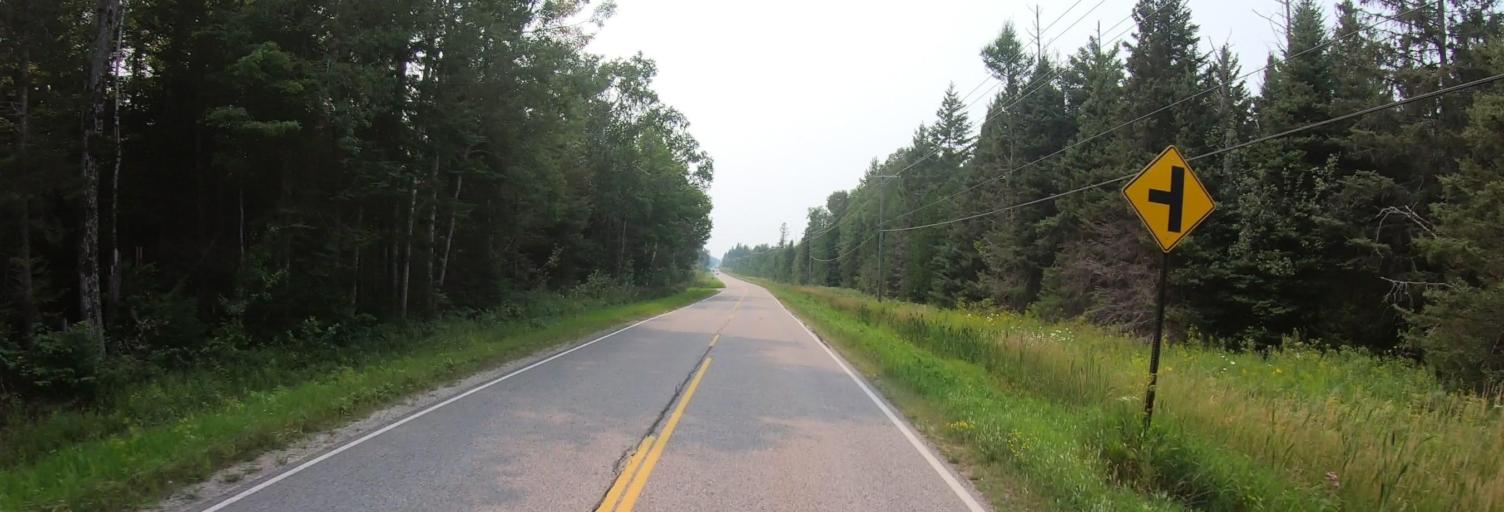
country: CA
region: Ontario
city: Thessalon
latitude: 46.0149
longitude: -84.0282
